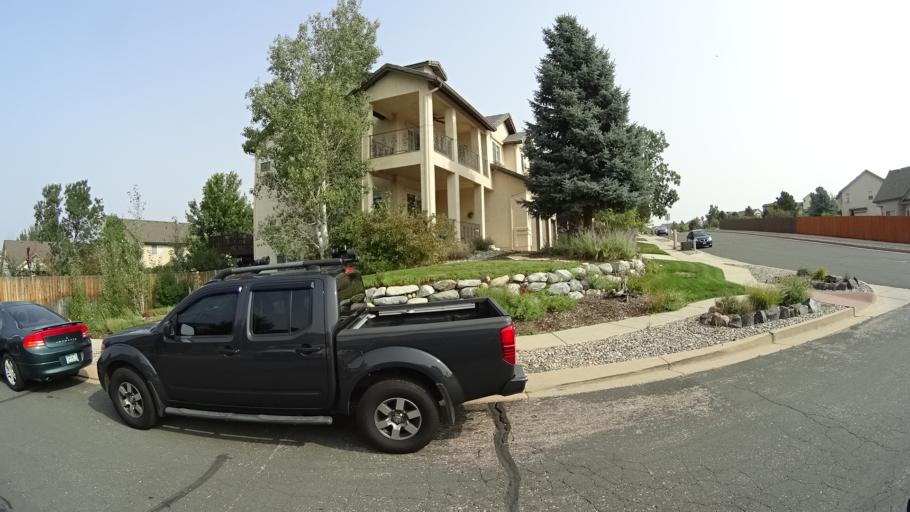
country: US
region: Colorado
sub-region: El Paso County
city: Cimarron Hills
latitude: 38.9300
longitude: -104.7393
